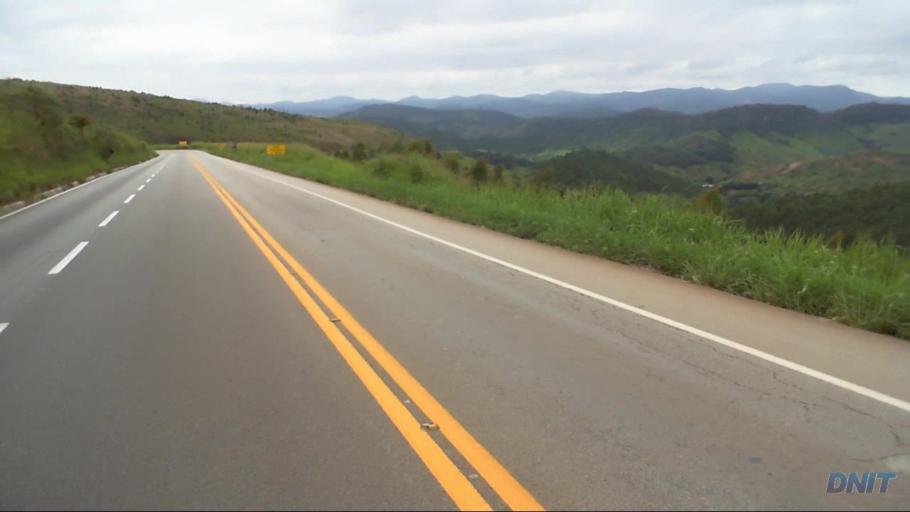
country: BR
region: Minas Gerais
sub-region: Nova Era
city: Nova Era
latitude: -19.8059
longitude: -43.0632
